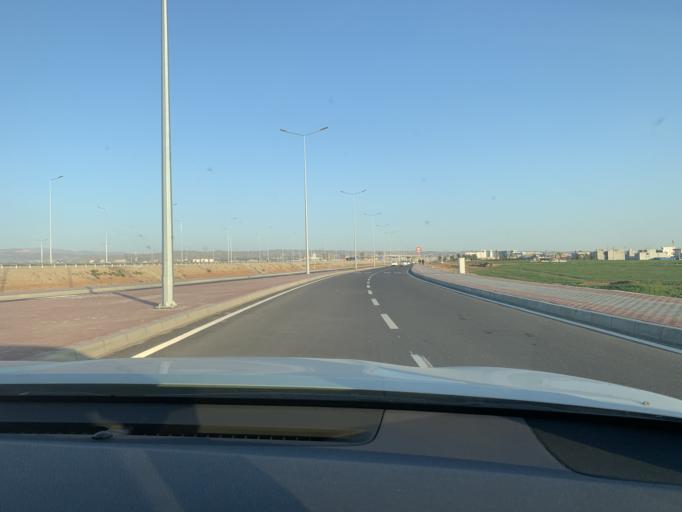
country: IQ
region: Arbil
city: Erbil
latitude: 36.2825
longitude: 44.0574
